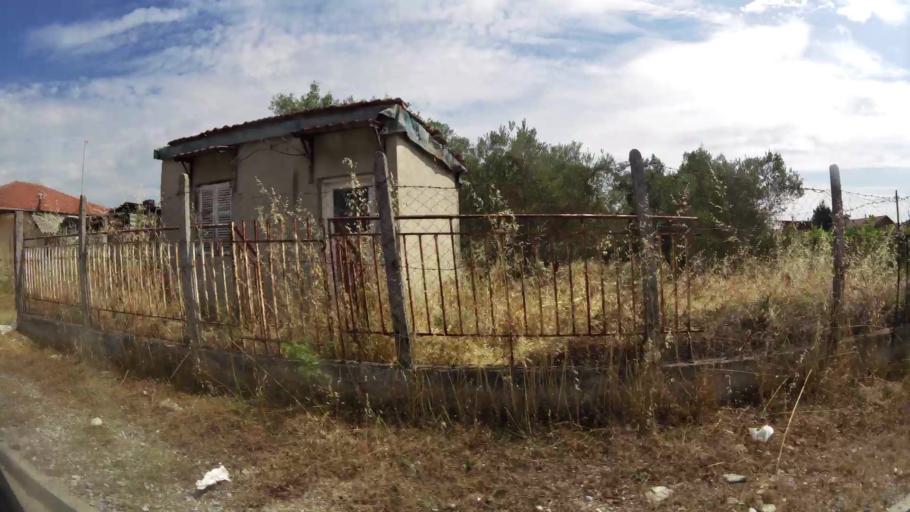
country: GR
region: Central Macedonia
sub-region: Nomos Pierias
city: Katerini
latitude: 40.2669
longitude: 22.4911
